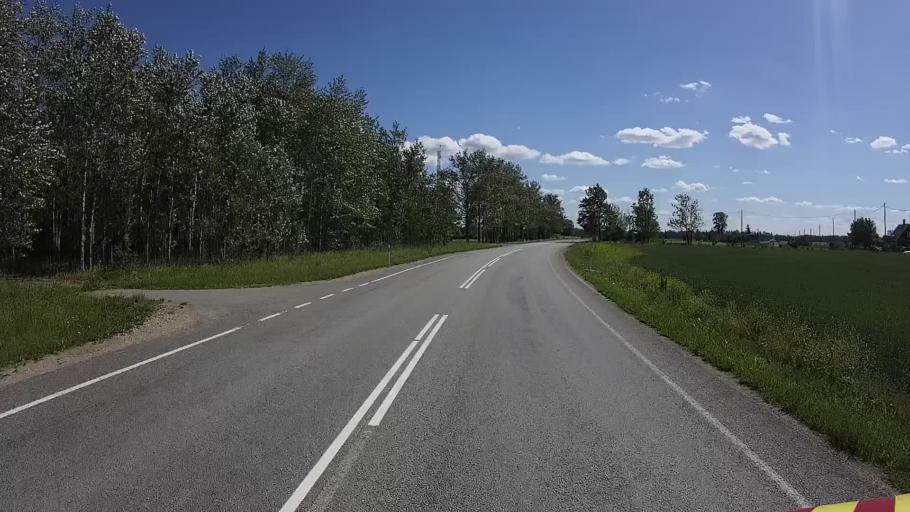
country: EE
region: Ida-Virumaa
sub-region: Johvi vald
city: Johvi
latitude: 59.3685
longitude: 27.3516
